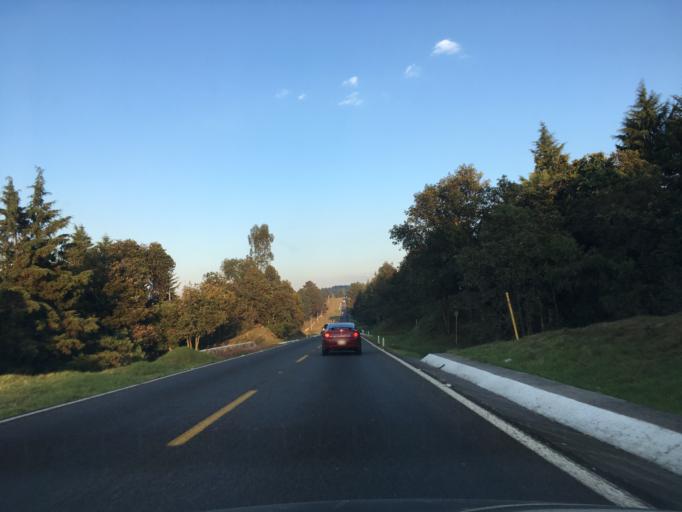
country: MX
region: Michoacan
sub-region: Patzcuaro
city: Santa Ana Chapitiro
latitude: 19.5095
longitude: -101.6819
